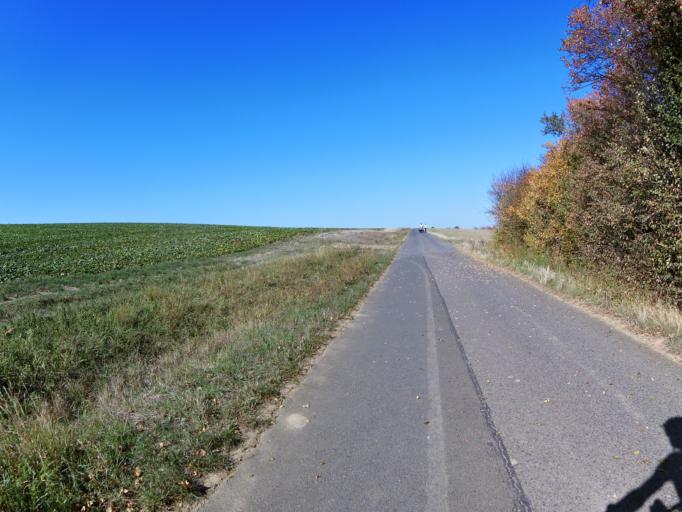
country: DE
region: Bavaria
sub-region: Regierungsbezirk Unterfranken
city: Eibelstadt
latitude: 49.7162
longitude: 9.9794
